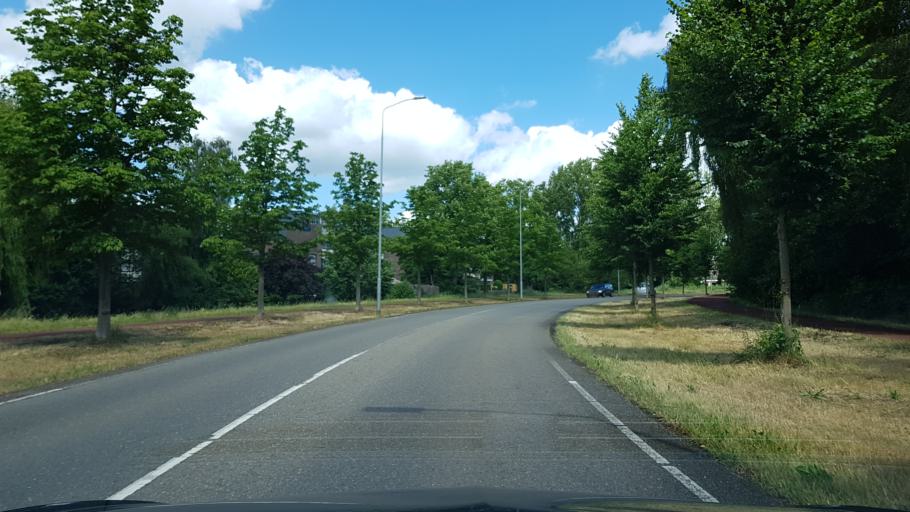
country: NL
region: Gelderland
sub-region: Gemeente Harderwijk
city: Harderwijk
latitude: 52.3391
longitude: 5.6130
